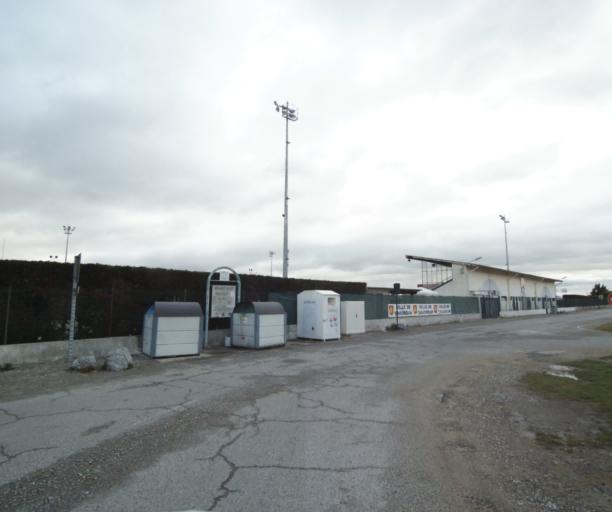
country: FR
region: Midi-Pyrenees
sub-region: Departement de l'Ariege
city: Saverdun
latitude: 43.2418
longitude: 1.5716
